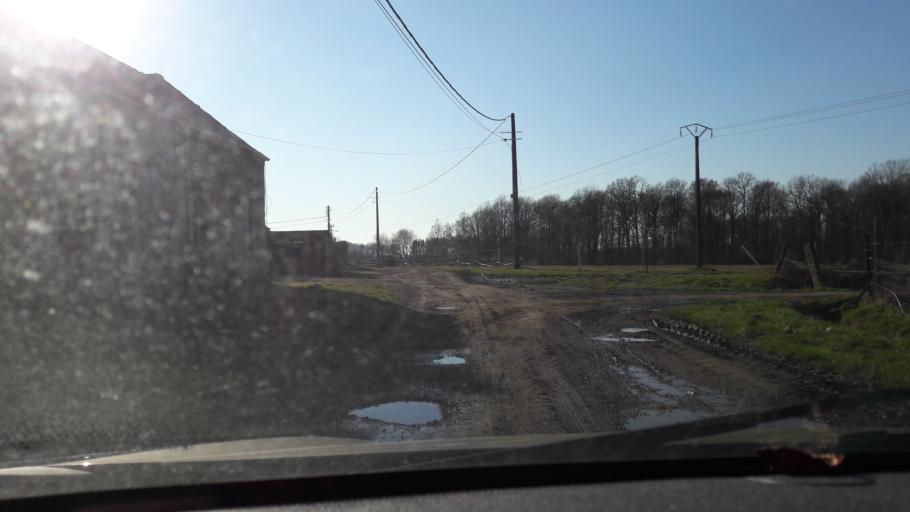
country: BE
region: Wallonia
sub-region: Province du Hainaut
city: Beaumont
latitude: 50.2506
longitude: 4.2039
